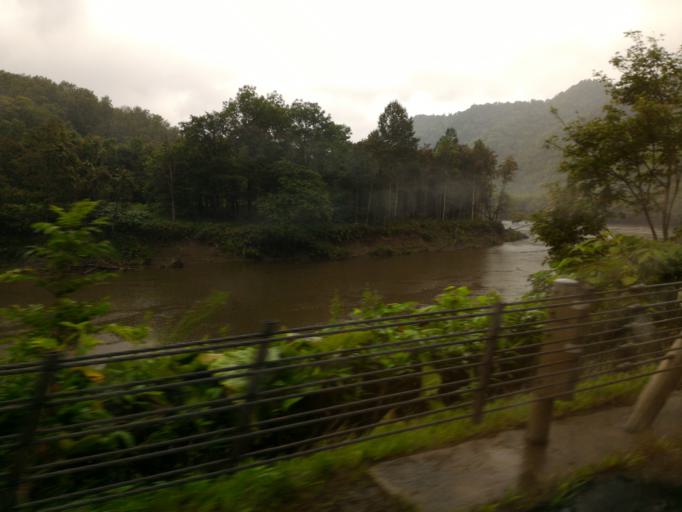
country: JP
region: Hokkaido
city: Nayoro
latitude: 44.7240
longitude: 142.1711
